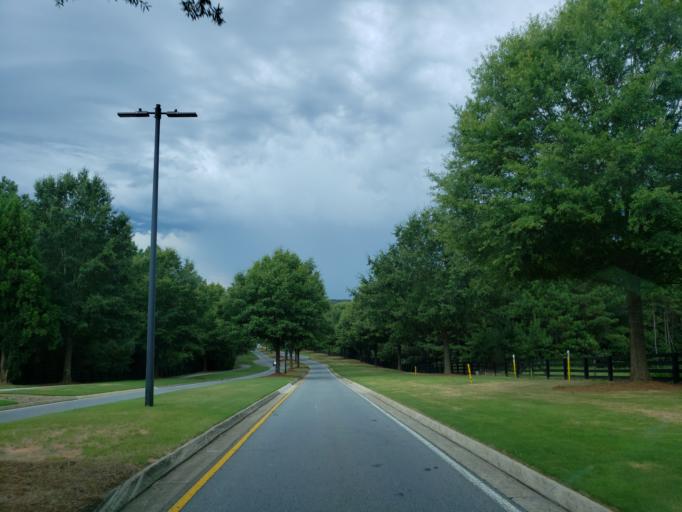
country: US
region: Georgia
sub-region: Bartow County
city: Emerson
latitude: 34.0275
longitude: -84.7784
